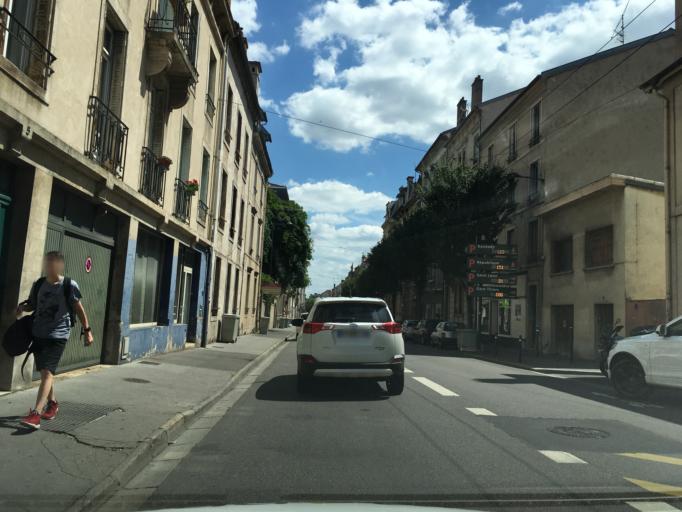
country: FR
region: Lorraine
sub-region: Departement de Meurthe-et-Moselle
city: Nancy
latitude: 48.6892
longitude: 6.1699
